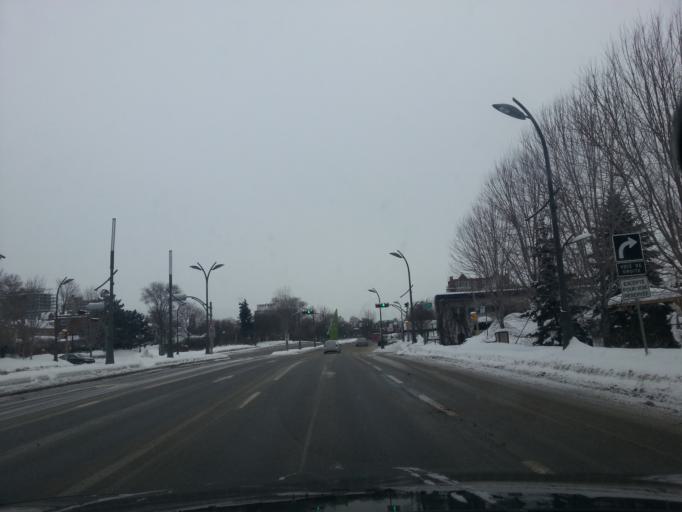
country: CA
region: Ontario
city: Ottawa
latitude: 45.4325
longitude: -75.7161
